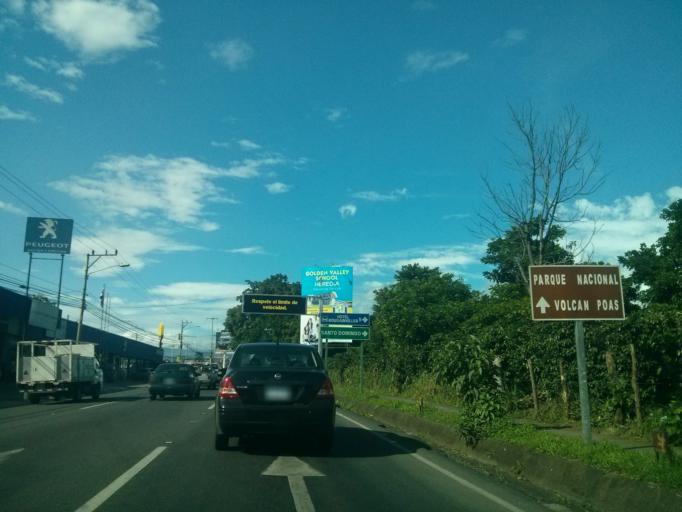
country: CR
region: Heredia
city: San Francisco
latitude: 9.9662
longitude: -84.1129
